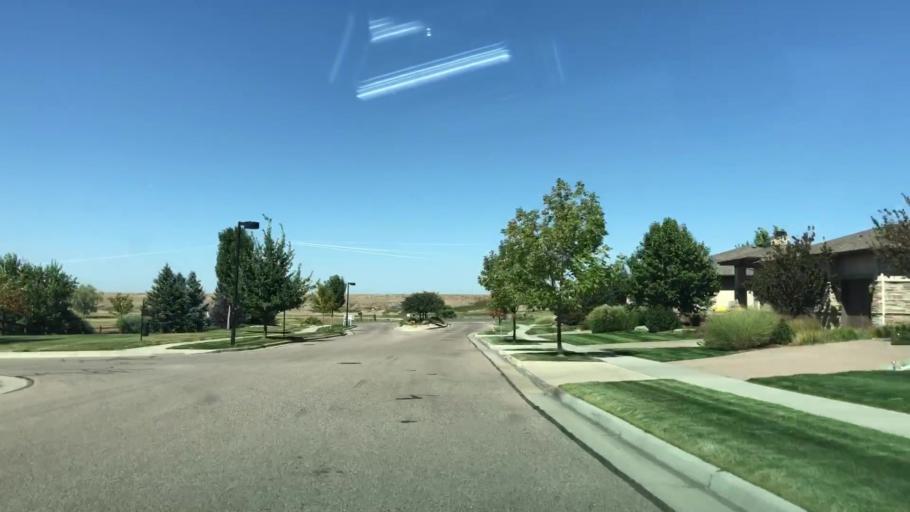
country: US
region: Colorado
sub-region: Weld County
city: Windsor
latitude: 40.5363
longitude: -104.9581
